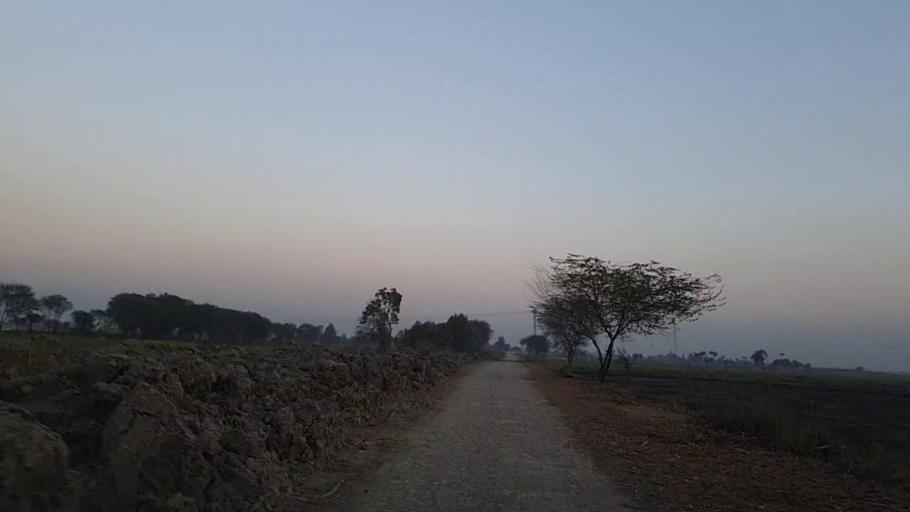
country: PK
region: Sindh
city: Naushahro Firoz
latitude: 26.7958
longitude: 68.0372
